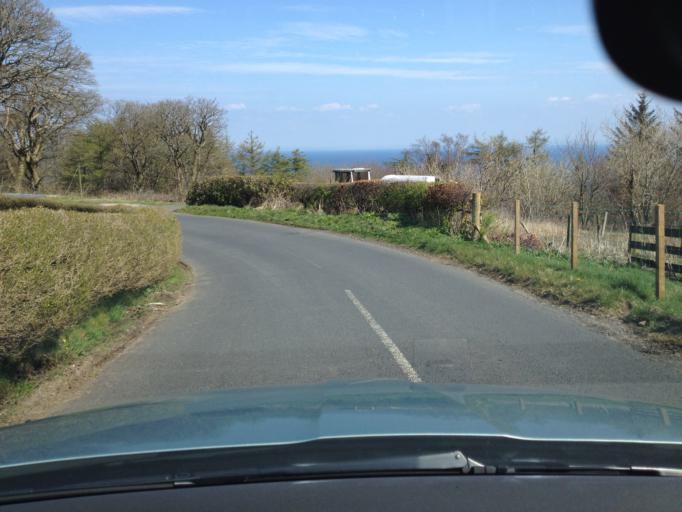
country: GB
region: Scotland
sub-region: North Ayrshire
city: Lamlash
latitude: 55.4570
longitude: -5.0897
